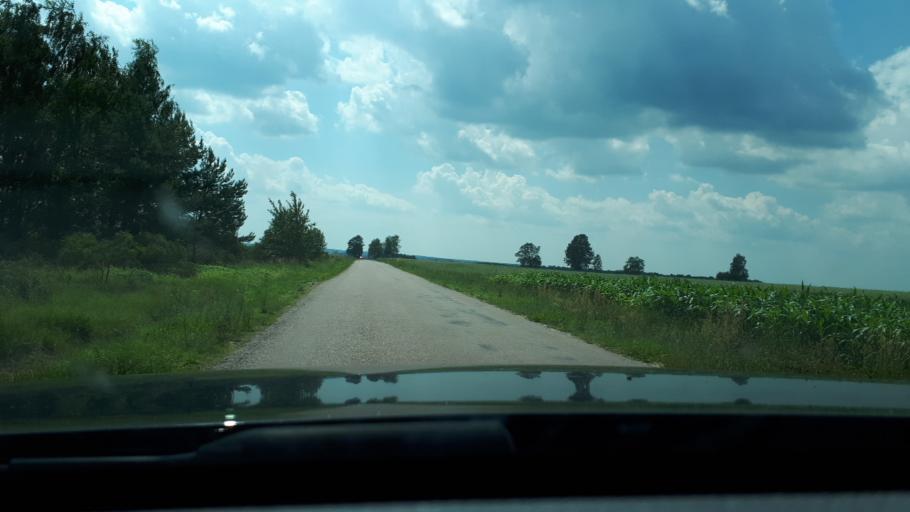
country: PL
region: Podlasie
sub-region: Powiat bialostocki
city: Lapy
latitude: 53.0976
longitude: 22.8604
